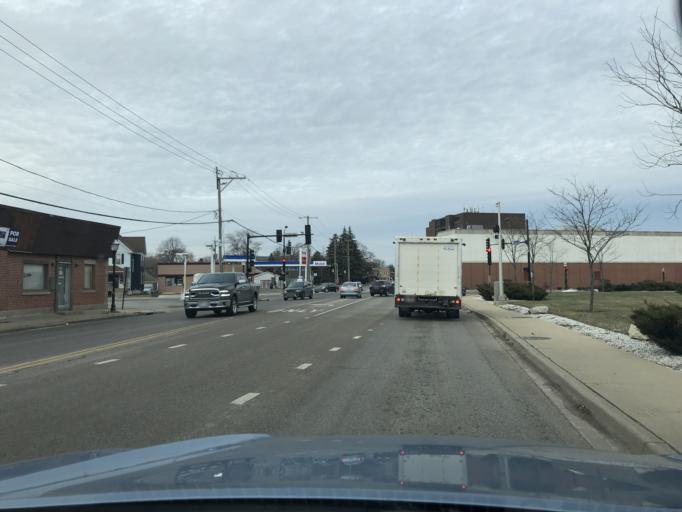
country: US
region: Illinois
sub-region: DuPage County
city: Bensenville
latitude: 41.9546
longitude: -87.9387
